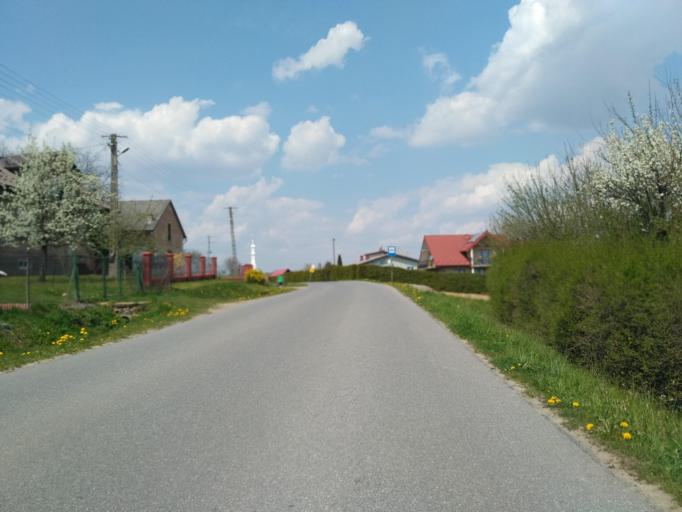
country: PL
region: Subcarpathian Voivodeship
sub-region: Powiat jasielski
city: Debowiec
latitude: 49.6968
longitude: 21.5086
